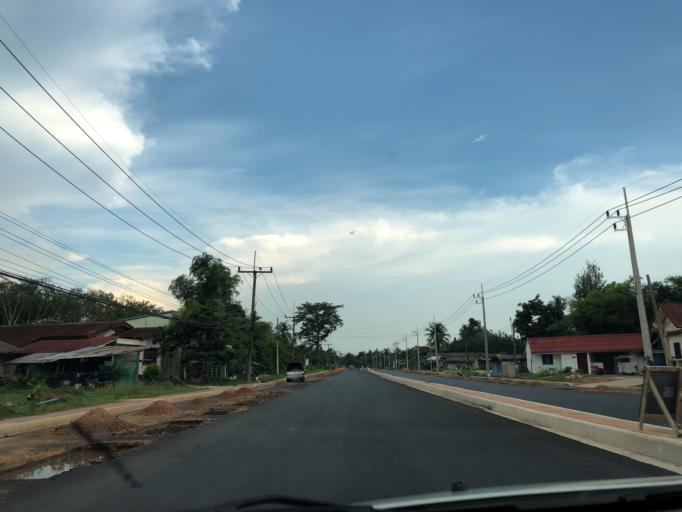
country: TH
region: Phangnga
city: Ban Ao Nang
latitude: 8.0697
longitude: 98.8412
